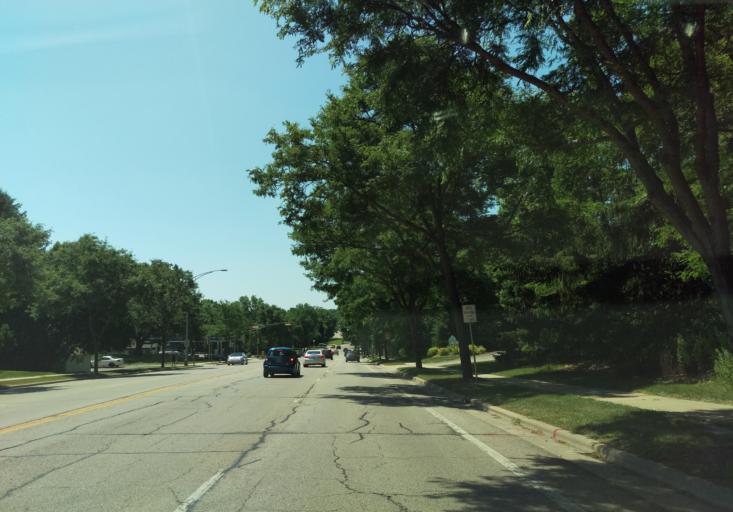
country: US
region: Wisconsin
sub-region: Dane County
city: Middleton
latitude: 43.0473
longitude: -89.5033
